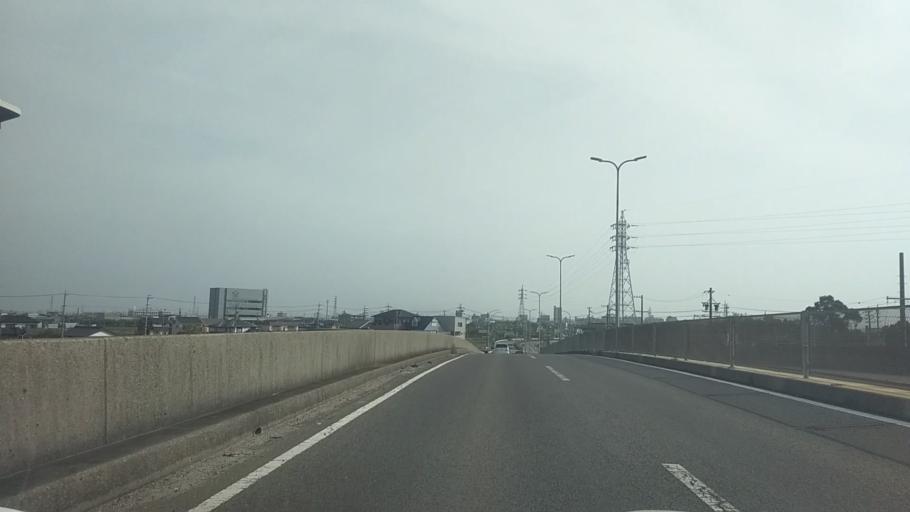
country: JP
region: Aichi
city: Anjo
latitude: 34.9659
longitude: 137.0724
